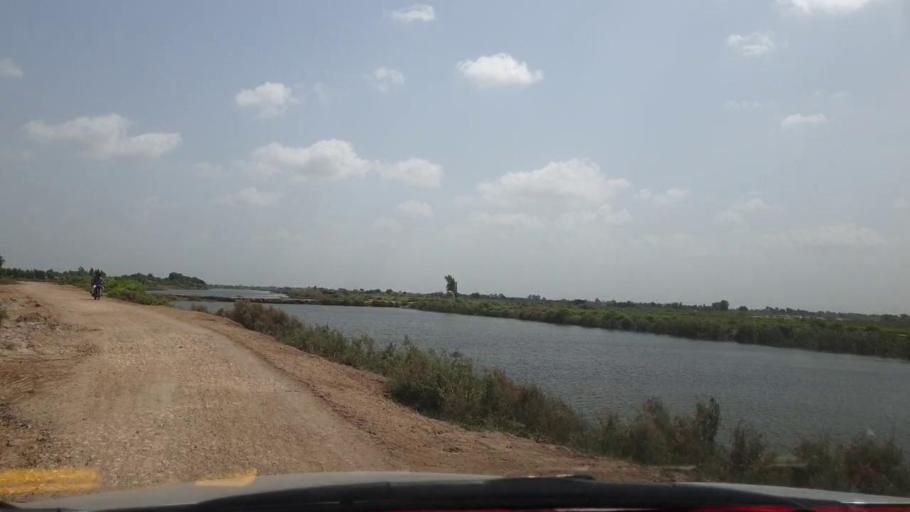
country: PK
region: Sindh
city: Talhar
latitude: 24.8766
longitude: 68.9112
